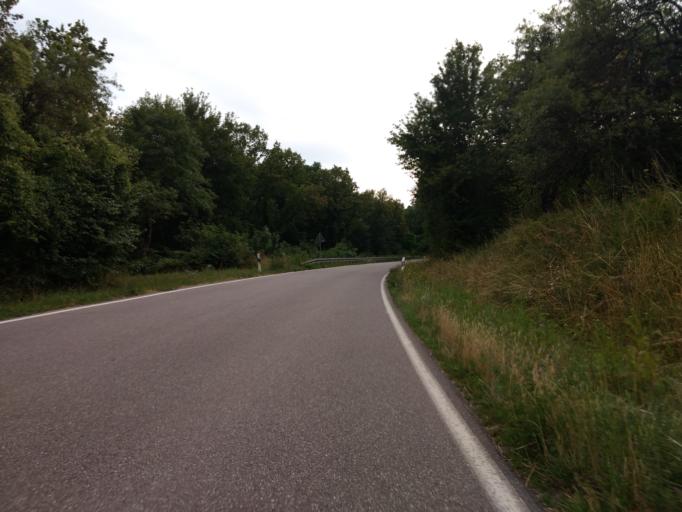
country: DE
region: Saarland
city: Rehlingen-Siersburg
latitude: 49.3294
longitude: 6.6263
